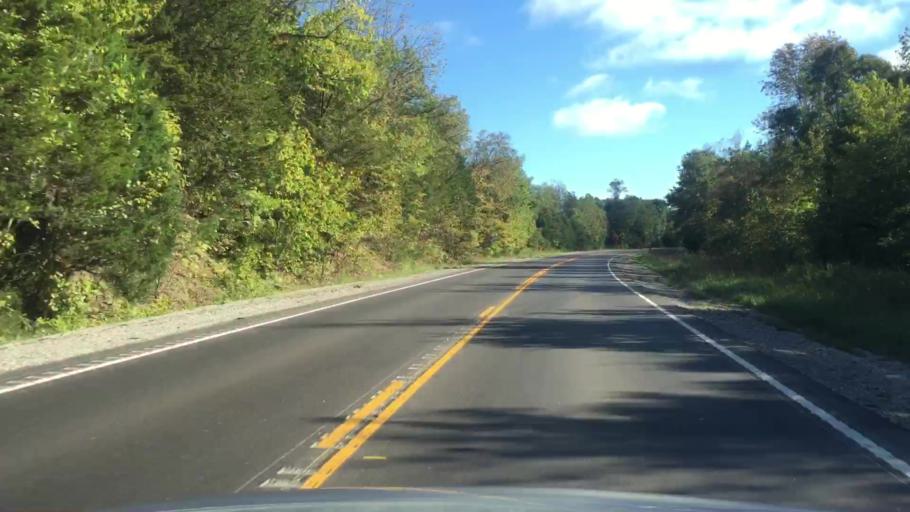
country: US
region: Missouri
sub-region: Boone County
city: Columbia
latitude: 38.9883
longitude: -92.5348
